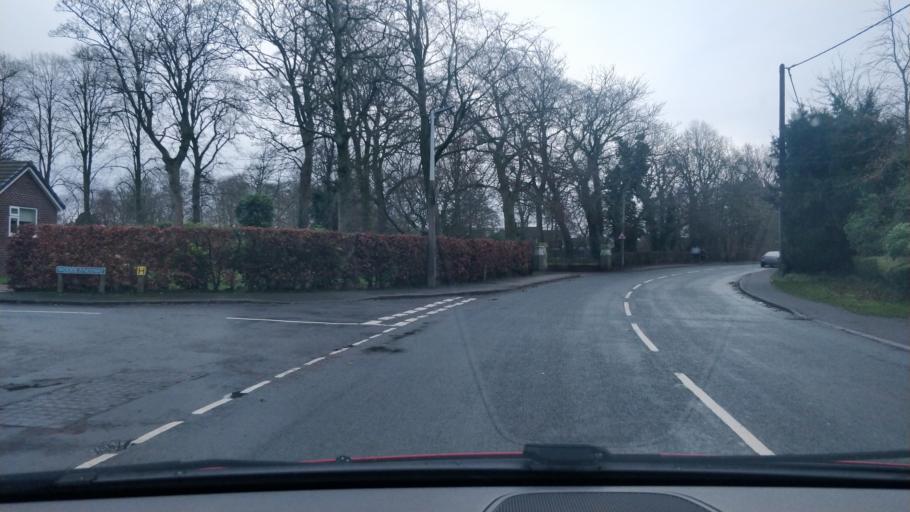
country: GB
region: England
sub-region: Lancashire
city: Tarleton
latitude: 53.7236
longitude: -2.7908
